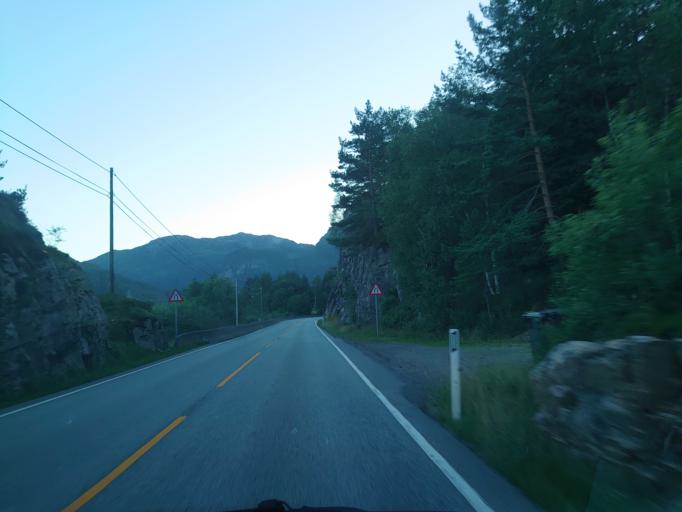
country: NO
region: Hordaland
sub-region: Osteroy
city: Lonevag
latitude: 60.7021
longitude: 5.6003
